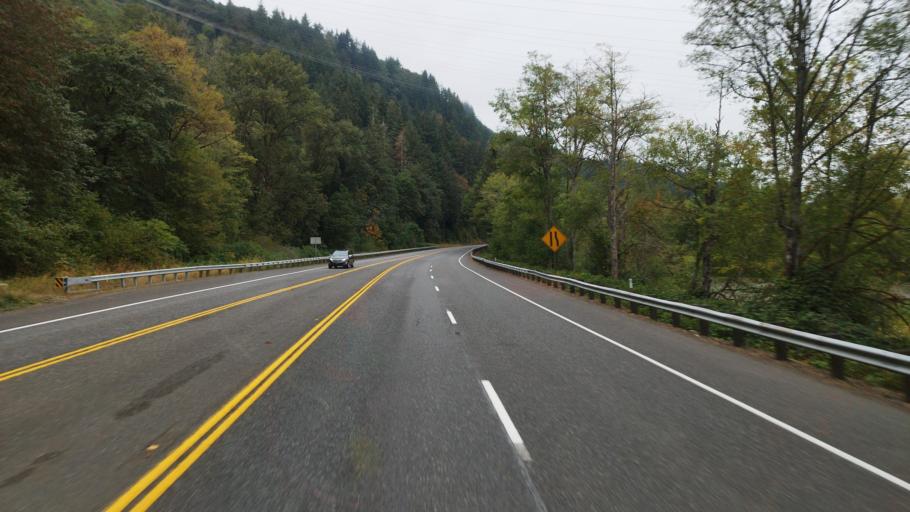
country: US
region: Washington
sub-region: Cowlitz County
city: Kalama
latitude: 46.0364
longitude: -122.8950
